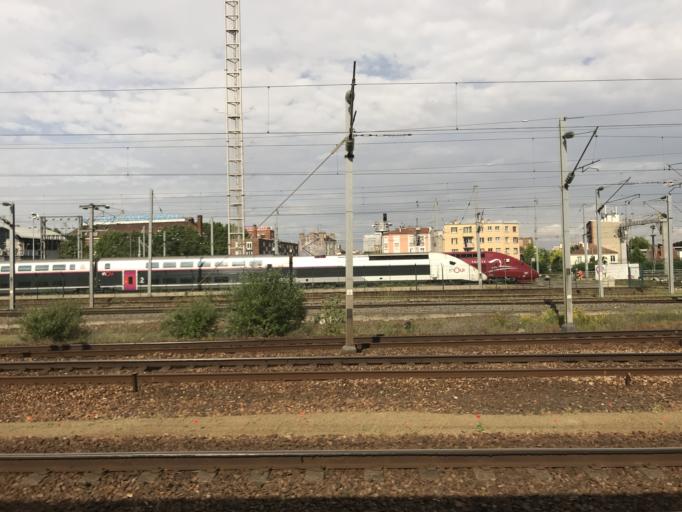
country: FR
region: Ile-de-France
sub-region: Paris
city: Saint-Ouen
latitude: 48.9029
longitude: 2.3533
